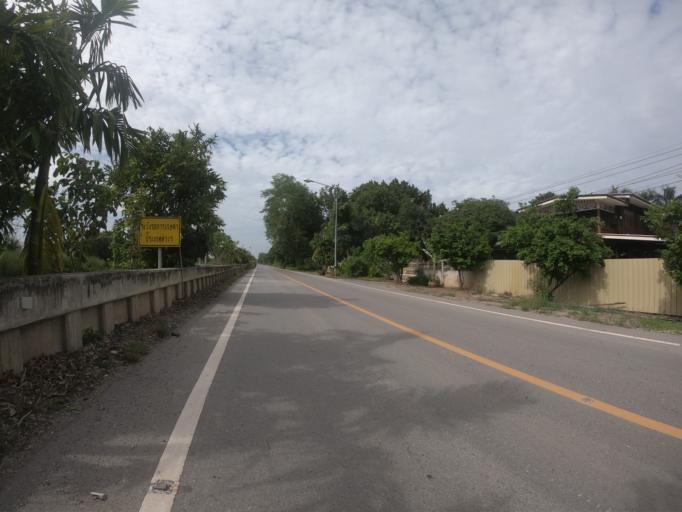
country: TH
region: Pathum Thani
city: Nong Suea
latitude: 14.0569
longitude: 100.8926
